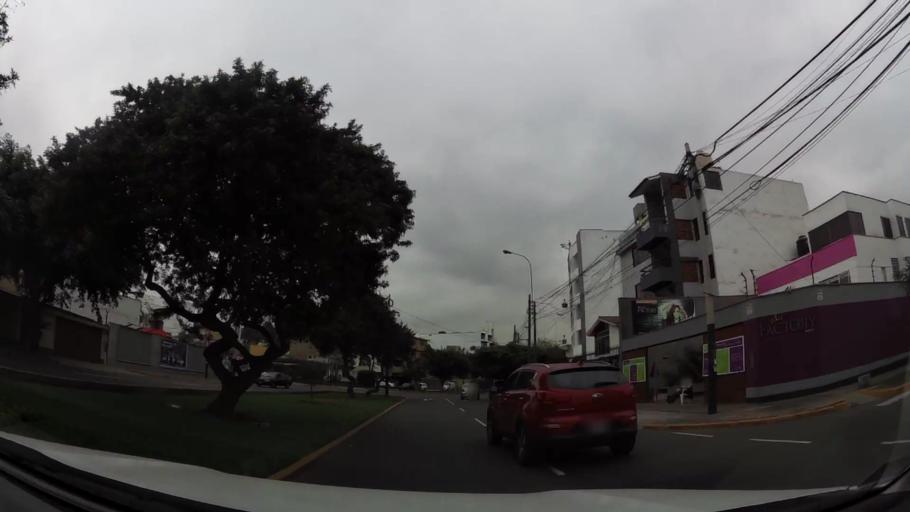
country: PE
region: Lima
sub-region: Lima
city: Surco
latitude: -12.1215
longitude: -76.9934
